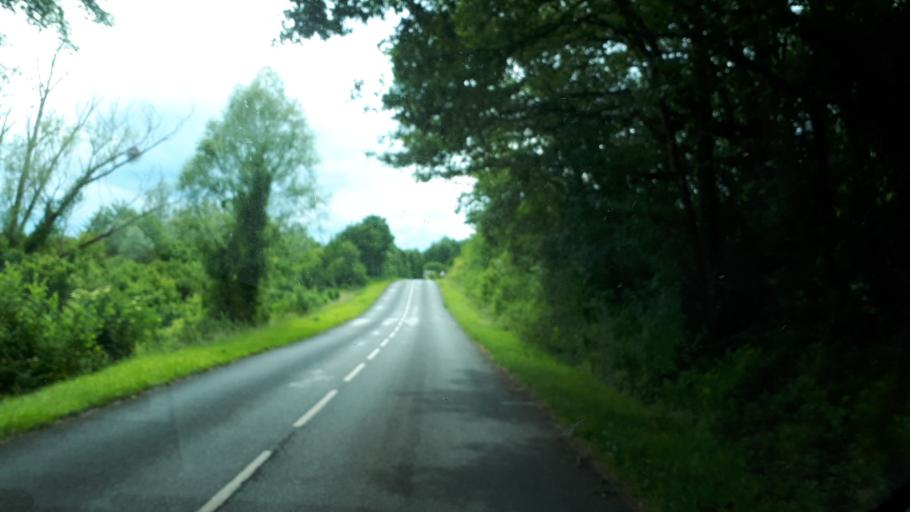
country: FR
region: Centre
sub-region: Departement du Cher
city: Gracay
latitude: 47.1376
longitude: 1.8686
